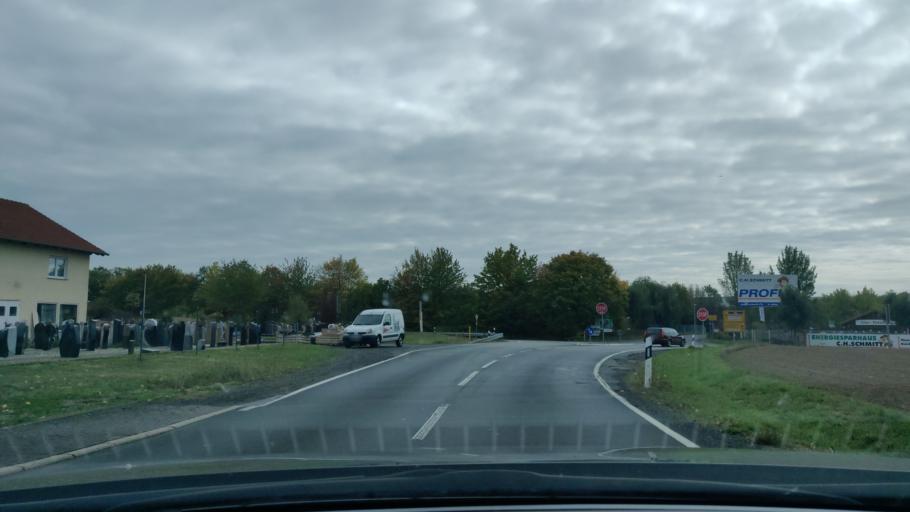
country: DE
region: Hesse
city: Schwalmstadt
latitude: 50.9226
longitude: 9.2244
